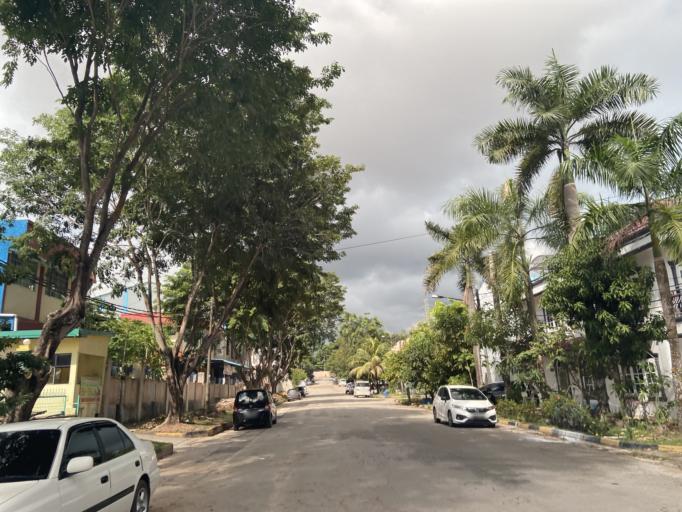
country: SG
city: Singapore
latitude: 1.1213
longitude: 104.0238
